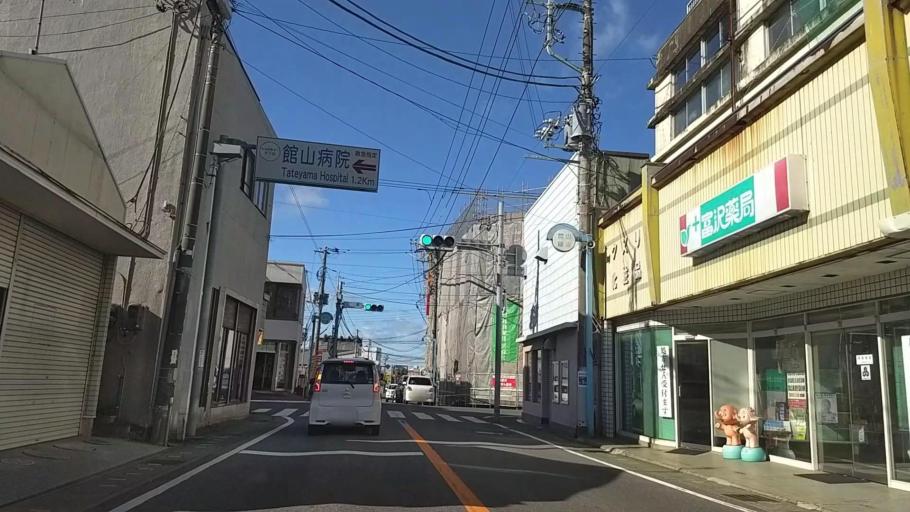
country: JP
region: Chiba
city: Tateyama
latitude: 34.9932
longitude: 139.8635
